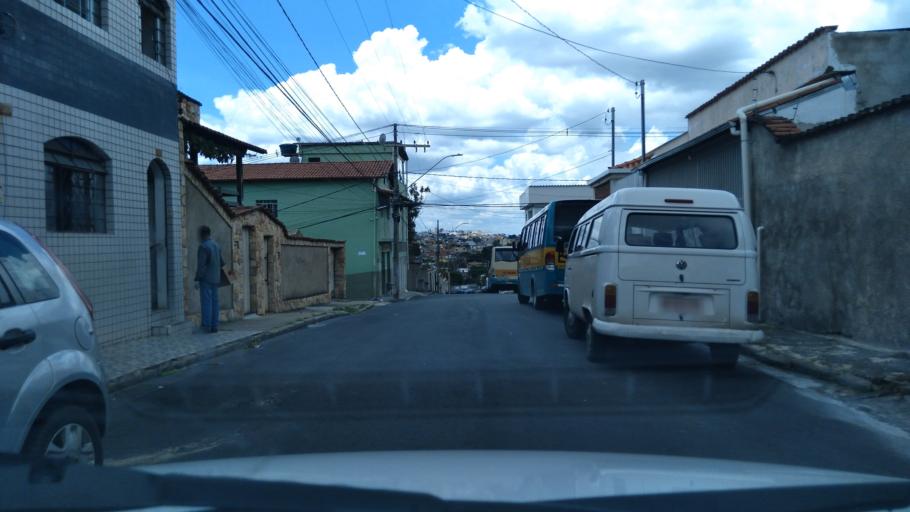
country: BR
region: Minas Gerais
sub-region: Belo Horizonte
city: Belo Horizonte
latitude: -19.9143
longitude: -43.8988
